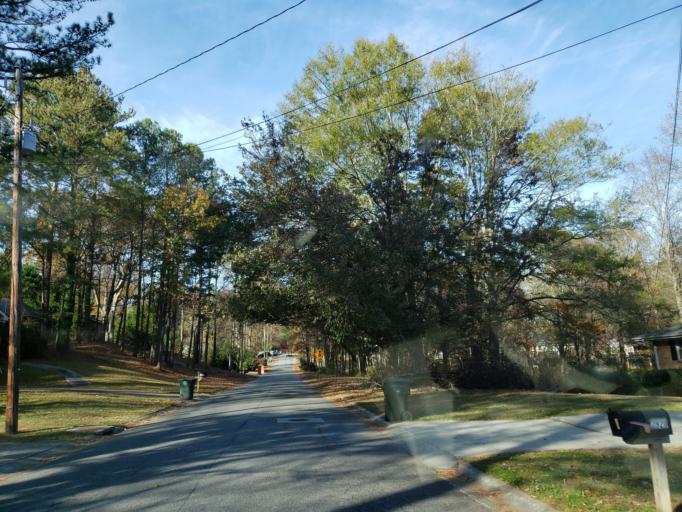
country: US
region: Georgia
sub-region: Cobb County
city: Kennesaw
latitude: 34.0246
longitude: -84.6070
